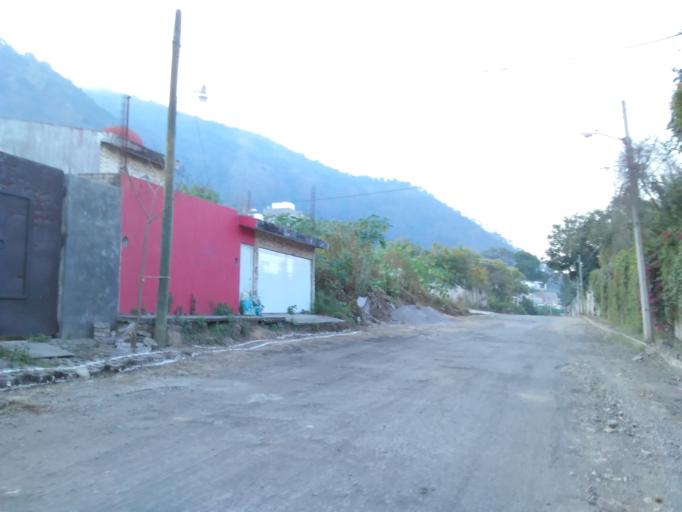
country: MX
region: Nayarit
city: Tepic
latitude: 21.5028
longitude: -104.9176
